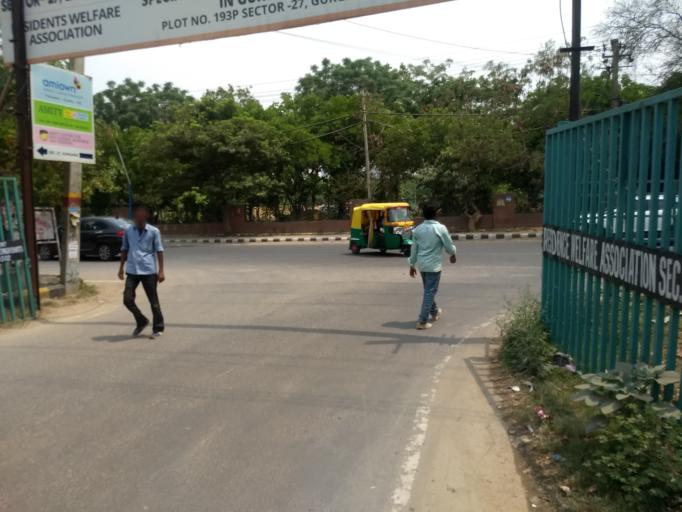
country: IN
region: Haryana
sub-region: Gurgaon
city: Gurgaon
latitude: 28.4628
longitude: 77.0917
